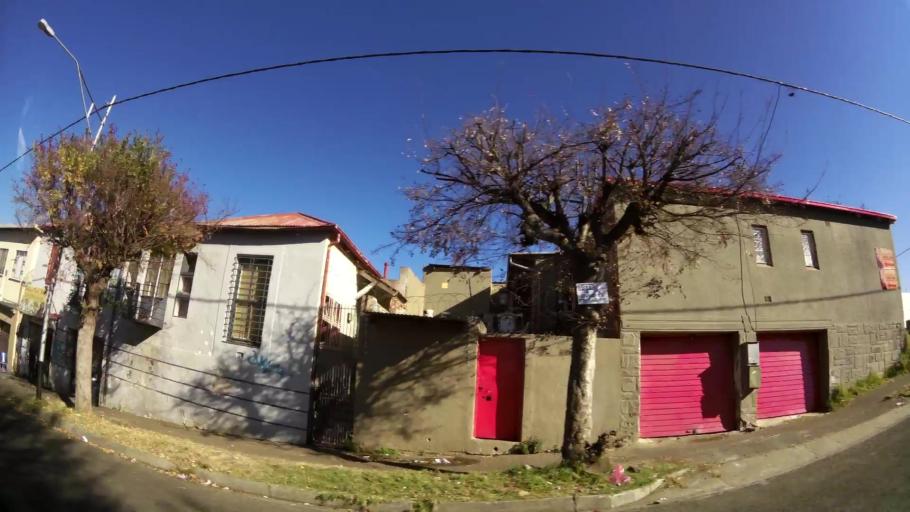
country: ZA
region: Gauteng
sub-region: City of Johannesburg Metropolitan Municipality
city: Johannesburg
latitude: -26.2007
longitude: 28.0058
